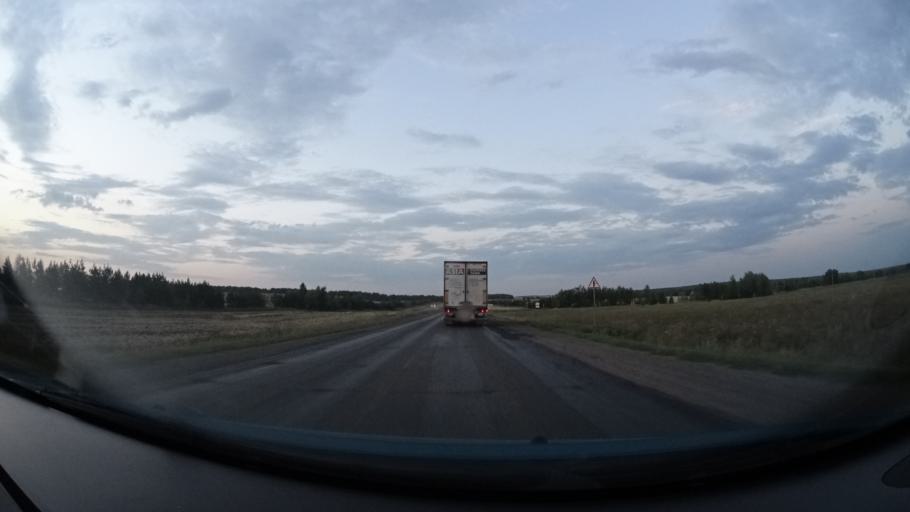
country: RU
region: Tatarstan
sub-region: Bavlinskiy Rayon
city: Bavly
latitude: 54.2756
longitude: 52.9841
